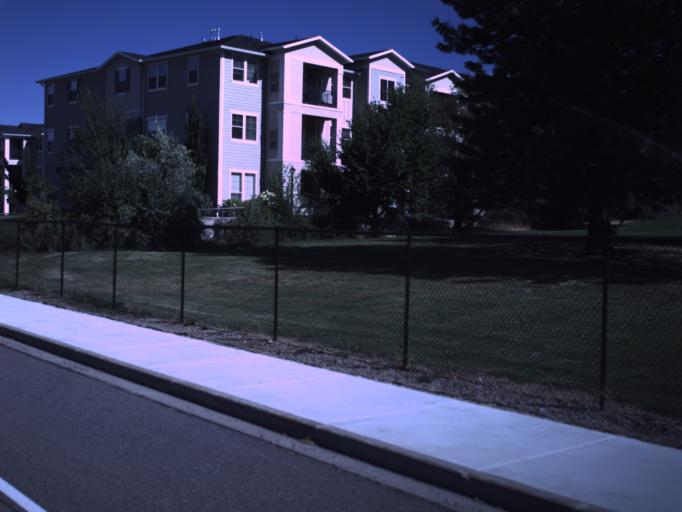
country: US
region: Utah
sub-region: Davis County
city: Kaysville
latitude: 41.0198
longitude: -111.9225
